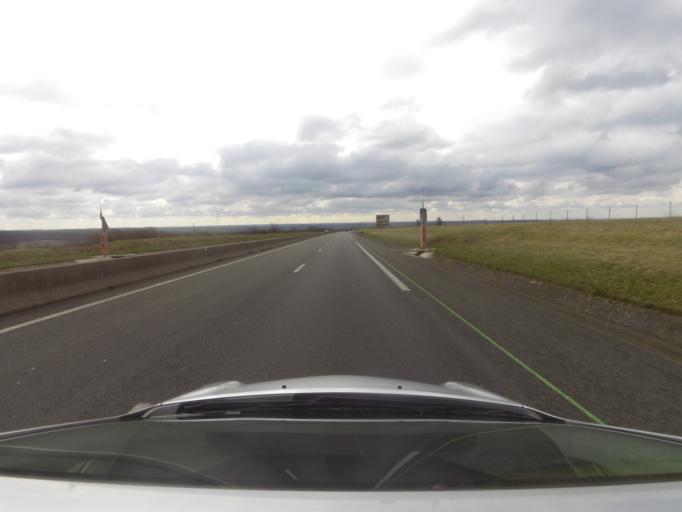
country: FR
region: Nord-Pas-de-Calais
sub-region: Departement du Pas-de-Calais
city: Etaples
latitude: 50.5505
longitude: 1.6731
